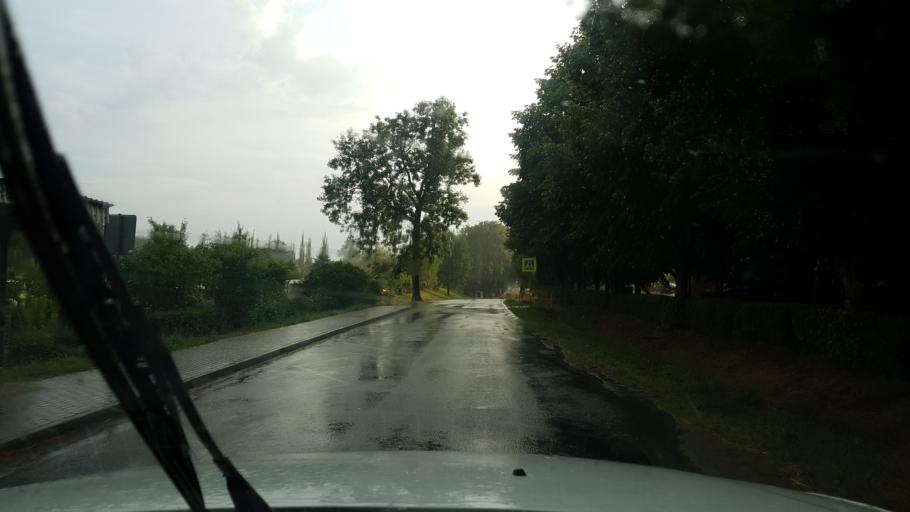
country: PL
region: West Pomeranian Voivodeship
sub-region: Powiat lobeski
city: Lobez
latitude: 53.6388
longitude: 15.6440
